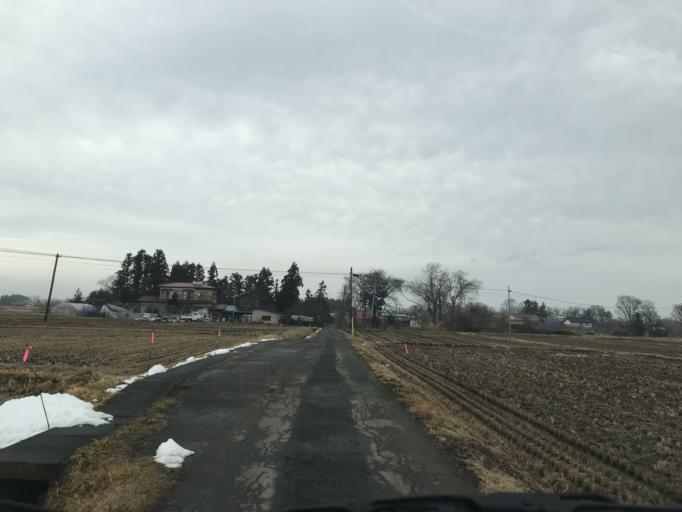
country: JP
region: Iwate
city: Mizusawa
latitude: 39.1788
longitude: 141.1389
